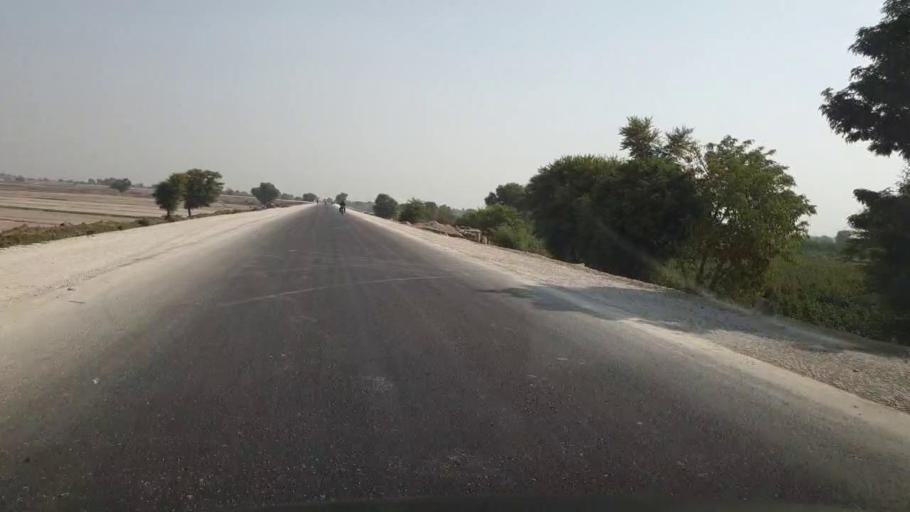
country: PK
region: Sindh
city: Bhan
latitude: 26.5560
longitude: 67.7772
